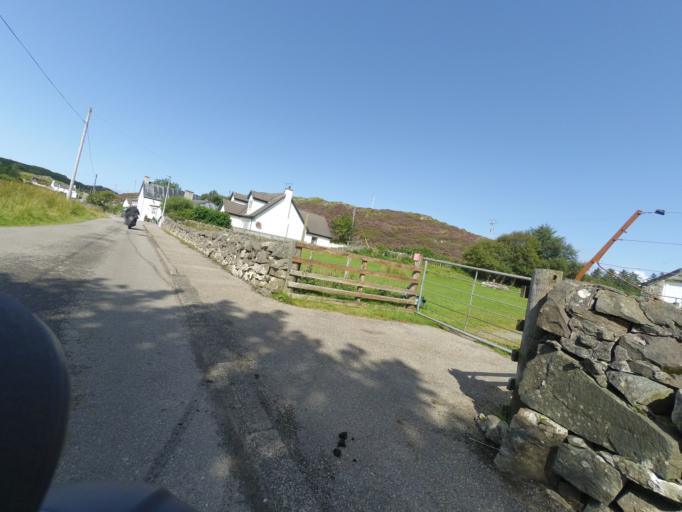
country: GB
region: Scotland
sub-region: Highland
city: Ullapool
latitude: 58.2427
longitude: -5.2010
